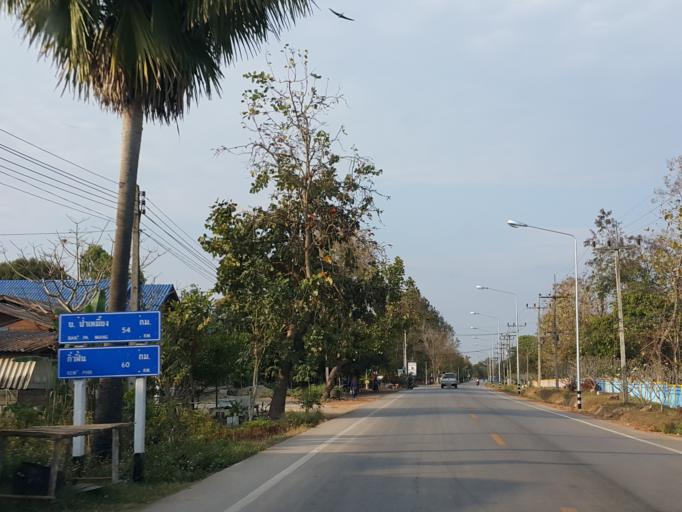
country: TH
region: Lampang
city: Chae Hom
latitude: 18.5331
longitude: 99.4782
